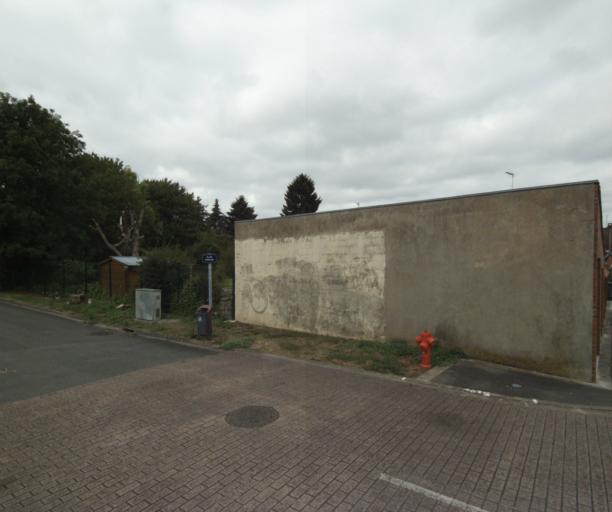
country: FR
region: Nord-Pas-de-Calais
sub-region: Departement du Nord
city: Lys-lez-Lannoy
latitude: 50.6754
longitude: 3.2277
